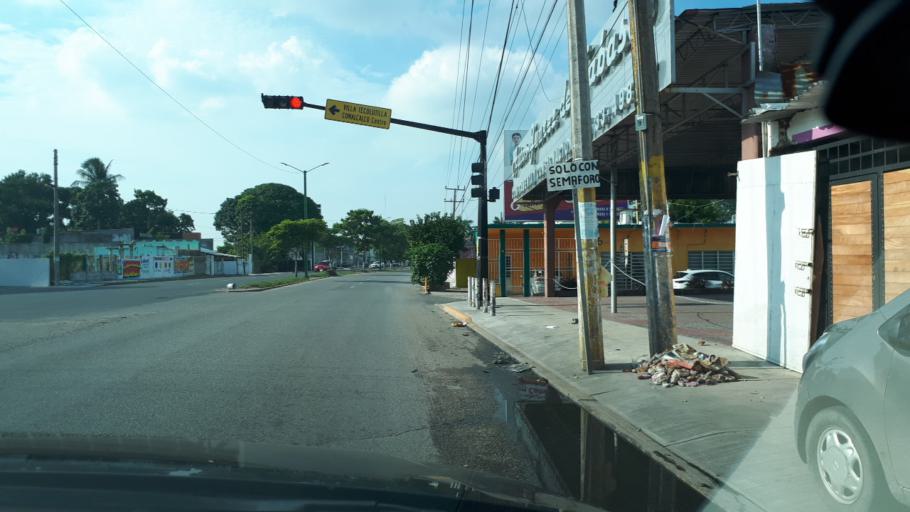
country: MX
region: Tabasco
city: Comalcalco
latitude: 18.2569
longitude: -93.2173
